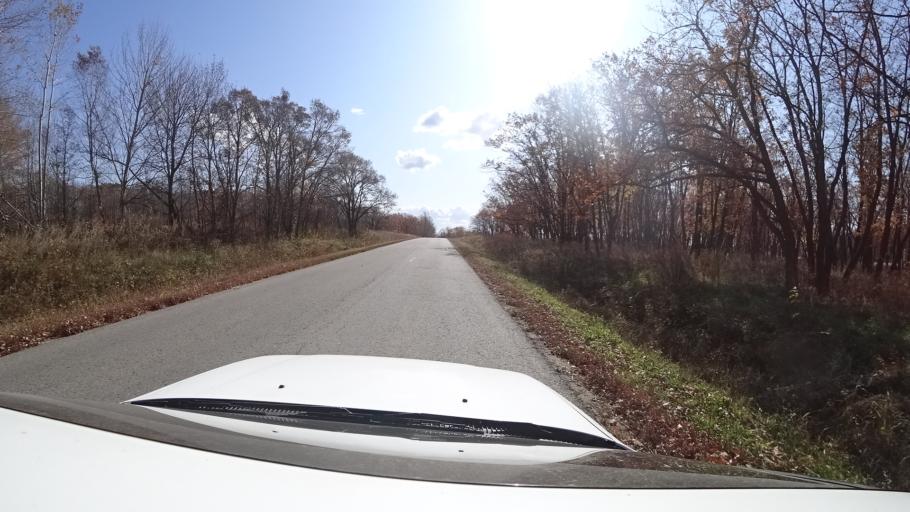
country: RU
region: Primorskiy
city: Lazo
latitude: 45.8695
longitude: 133.6610
